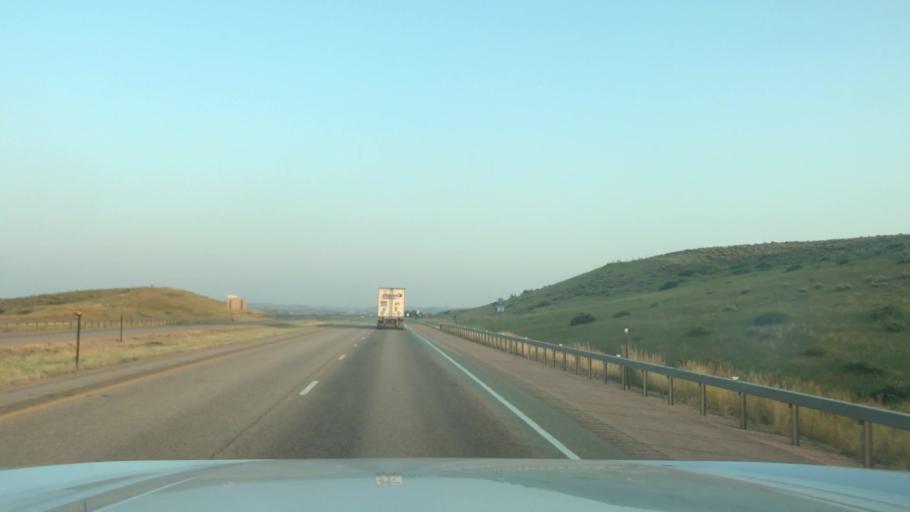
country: US
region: Wyoming
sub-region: Sheridan County
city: Sheridan
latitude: 44.8758
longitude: -106.9985
